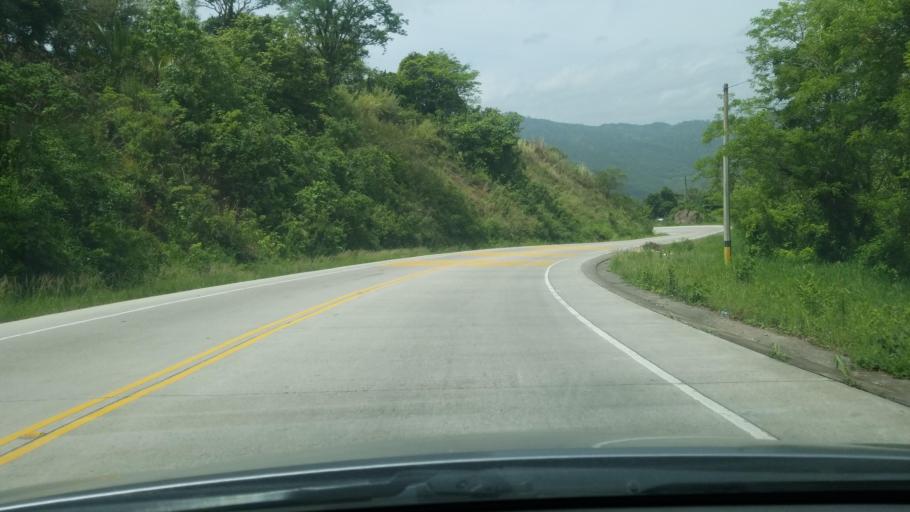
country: HN
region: Copan
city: Veracruz
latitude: 14.9133
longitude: -88.7536
